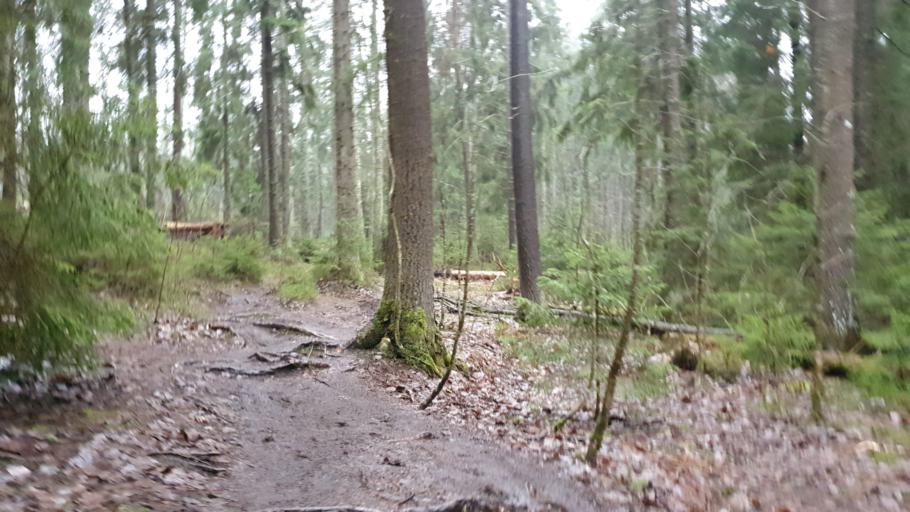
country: FI
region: Uusimaa
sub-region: Helsinki
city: Helsinki
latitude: 60.2636
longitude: 24.9206
